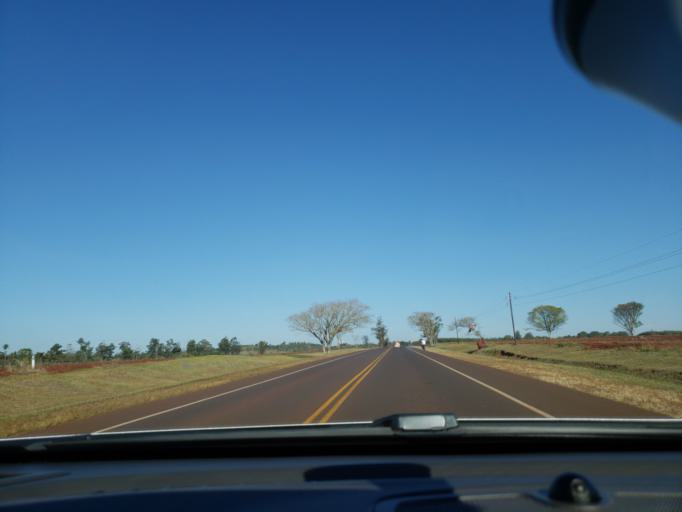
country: AR
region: Misiones
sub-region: Departamento de Apostoles
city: San Jose
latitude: -27.7848
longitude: -55.7724
